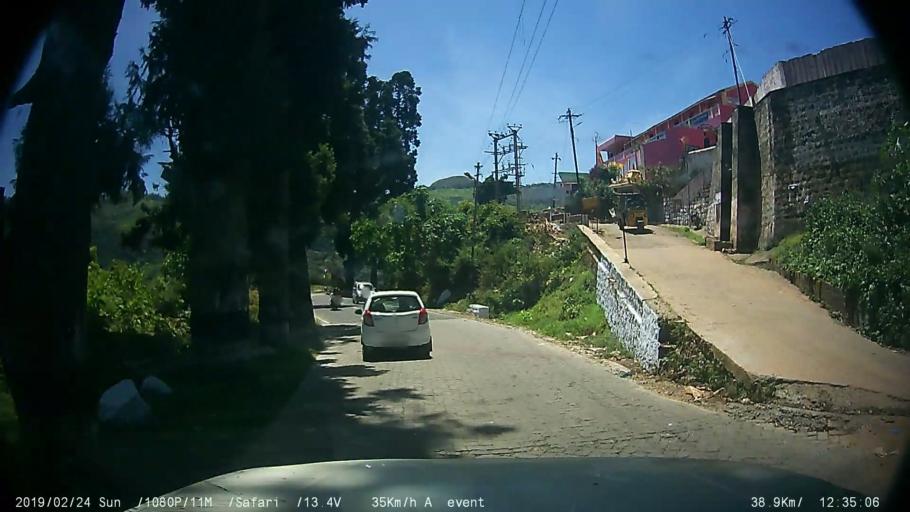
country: IN
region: Tamil Nadu
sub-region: Nilgiri
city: Wellington
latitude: 11.3352
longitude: 76.7987
